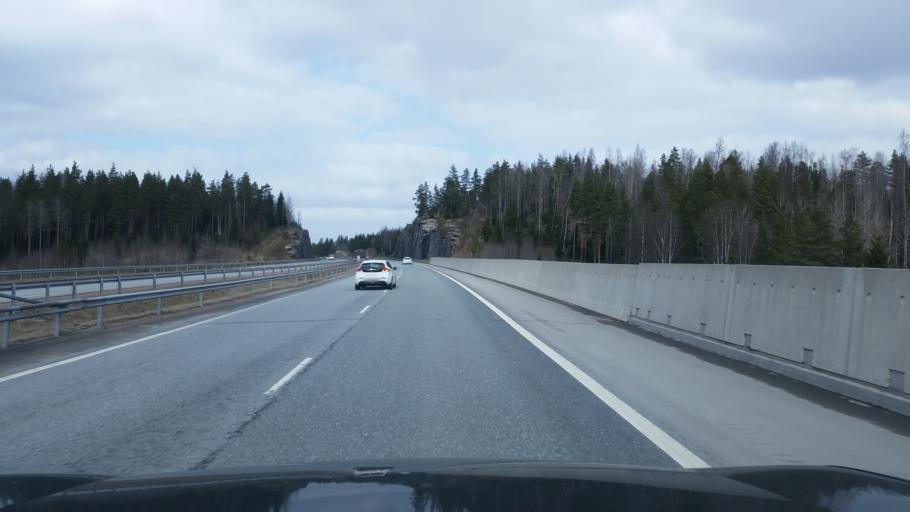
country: FI
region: Uusimaa
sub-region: Helsinki
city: Sammatti
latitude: 60.3570
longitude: 23.8906
